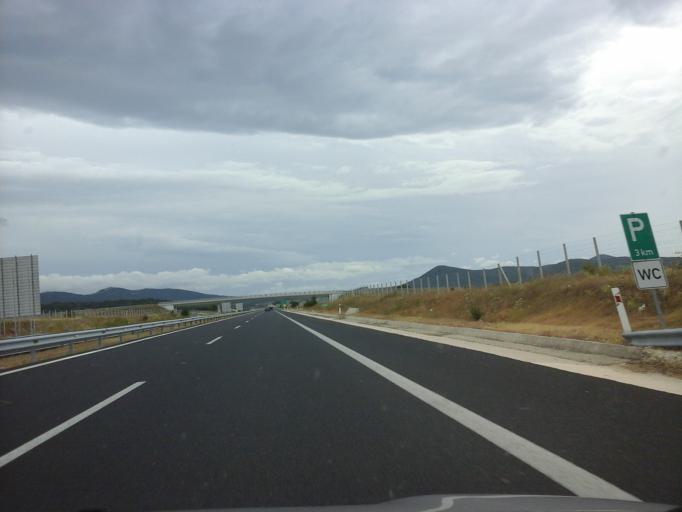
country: GR
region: East Macedonia and Thrace
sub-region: Nomos Evrou
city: Alexandroupoli
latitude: 40.9118
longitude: 25.9561
